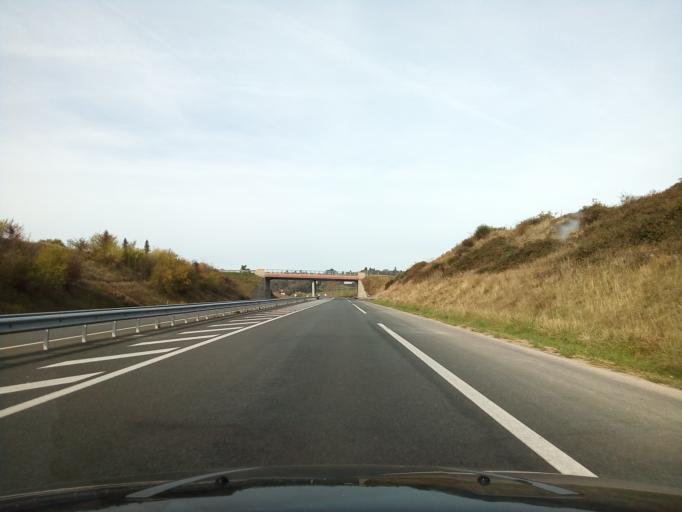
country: FR
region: Rhone-Alpes
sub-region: Departement de la Loire
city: La Pacaudiere
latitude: 46.1894
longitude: 3.8618
